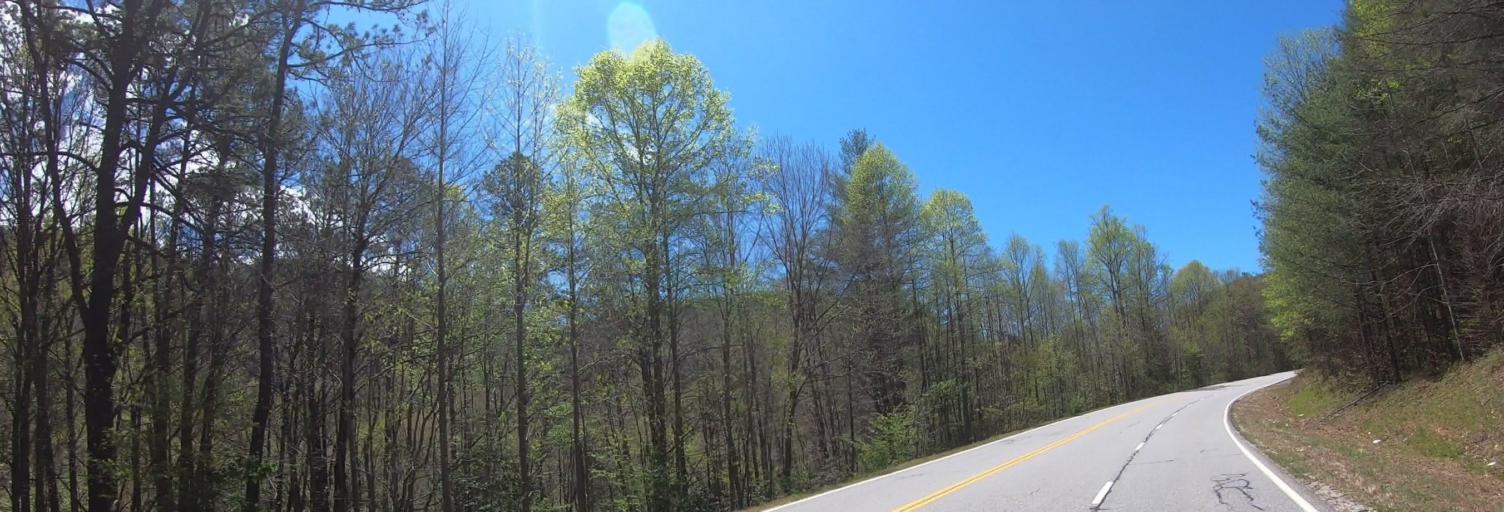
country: US
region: Georgia
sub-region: Towns County
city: Hiawassee
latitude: 34.8244
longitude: -83.7340
